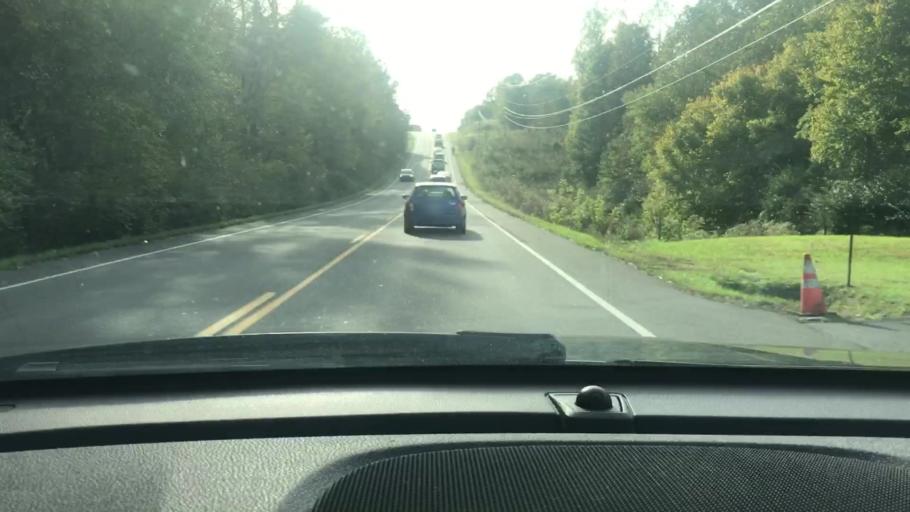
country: US
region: Tennessee
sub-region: Williamson County
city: Fairview
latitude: 35.9875
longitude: -87.1043
